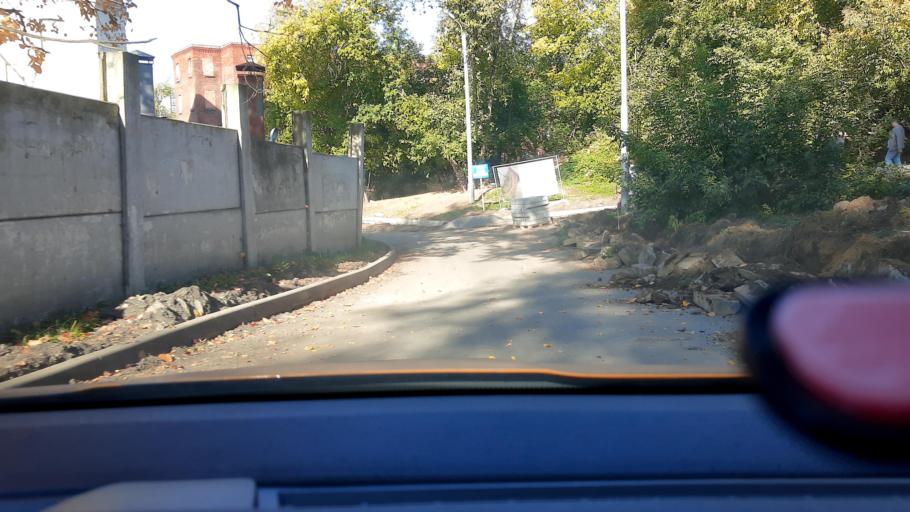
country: RU
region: Moscow
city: Strogino
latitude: 55.8385
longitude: 37.4132
